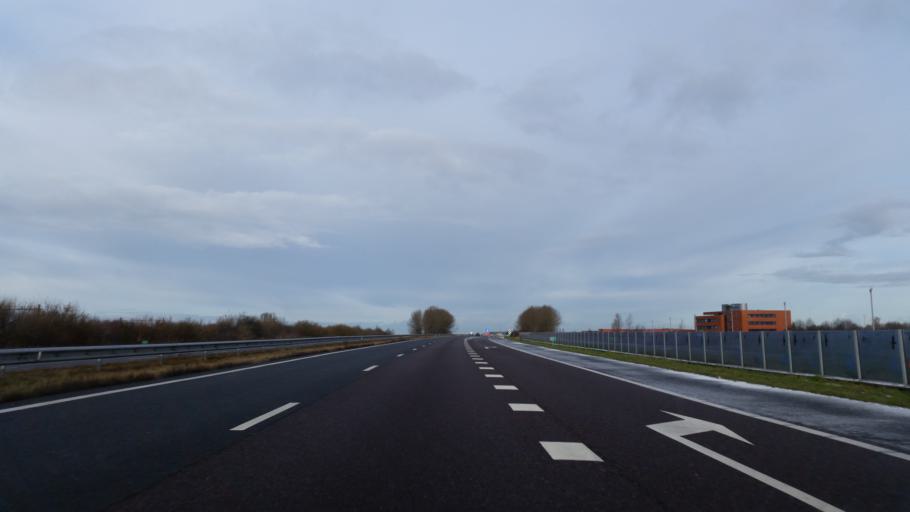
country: NL
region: Friesland
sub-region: Gemeente Boarnsterhim
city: Grou
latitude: 53.0847
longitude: 5.8263
